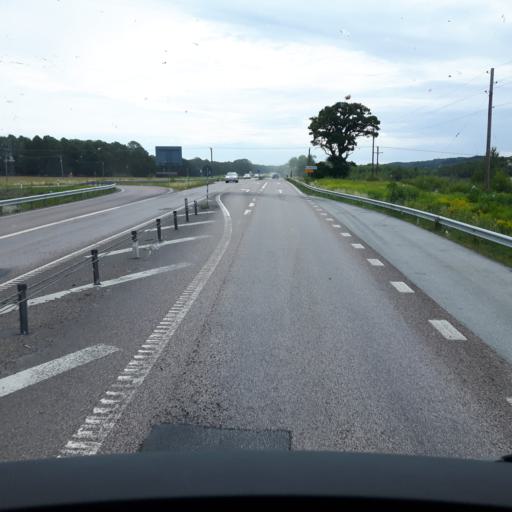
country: SE
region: Skane
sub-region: Hassleholms Kommun
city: Vinslov
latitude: 56.1134
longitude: 13.8586
